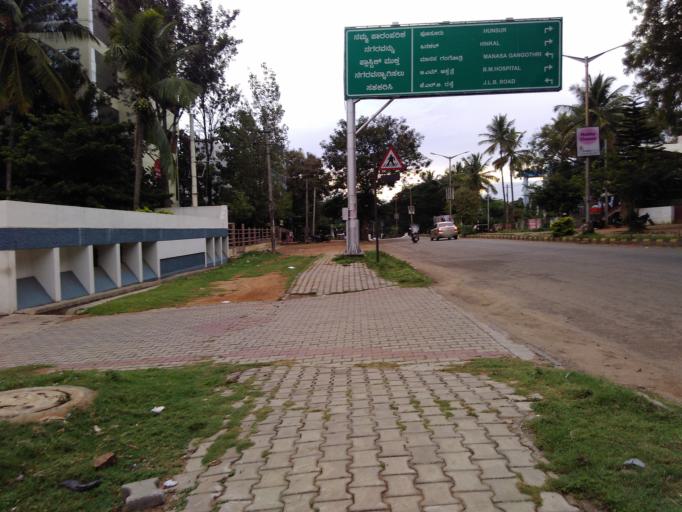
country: IN
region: Karnataka
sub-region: Mysore
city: Mysore
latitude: 12.3191
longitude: 76.6259
